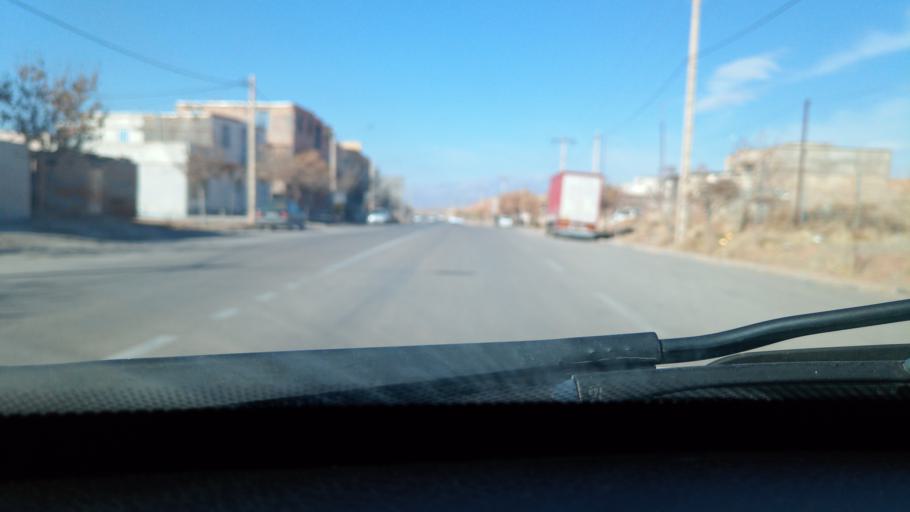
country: IR
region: Khorasan-e Shomali
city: Esfarayen
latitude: 37.0870
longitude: 57.4974
